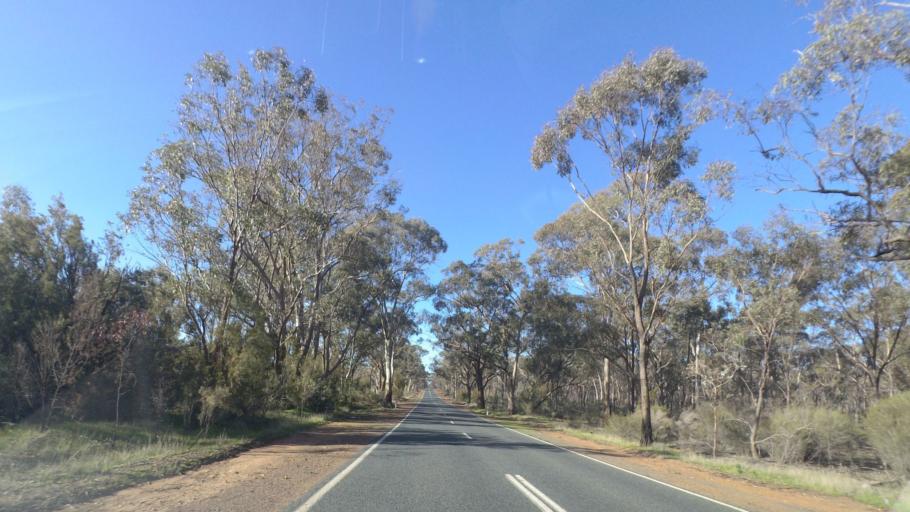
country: AU
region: Victoria
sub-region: Greater Bendigo
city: Epsom
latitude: -36.6699
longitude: 144.4196
